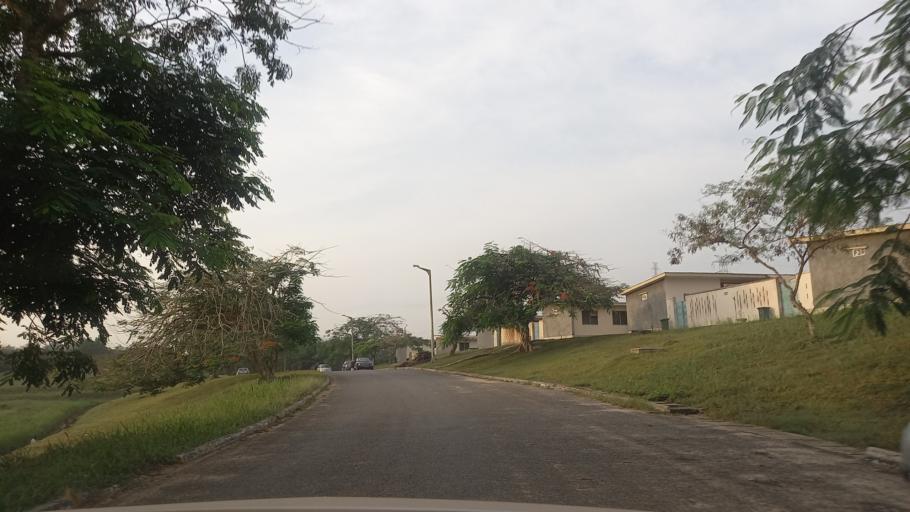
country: GH
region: Western
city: Shama Junction
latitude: 4.9825
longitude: -1.6600
